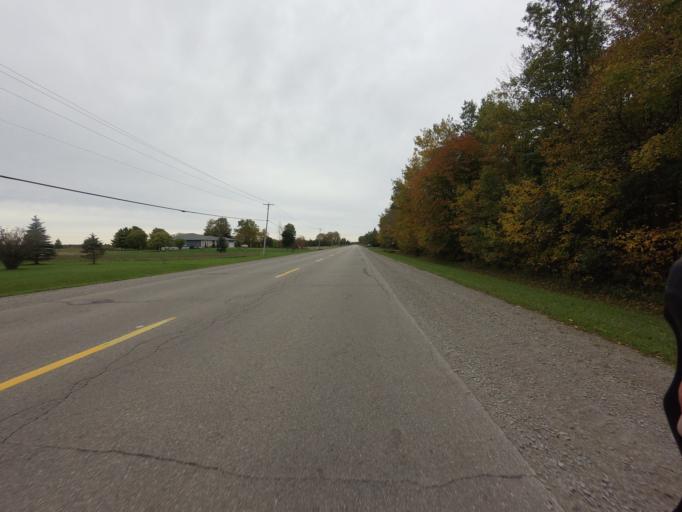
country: CA
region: Ontario
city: Brockville
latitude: 44.6394
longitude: -75.9190
